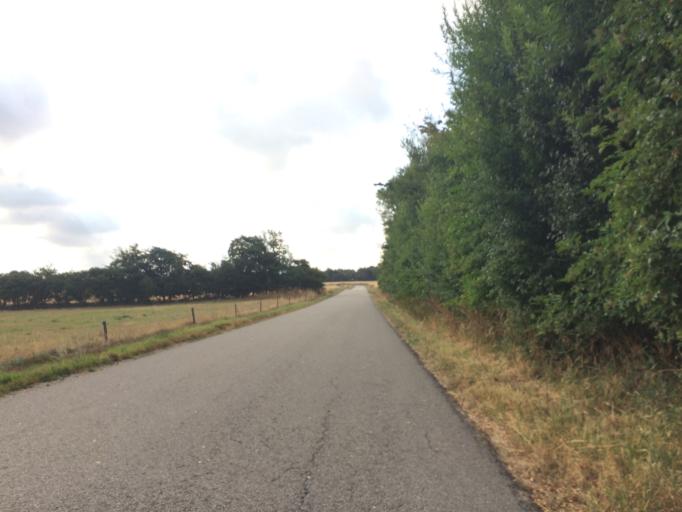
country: DK
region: Central Jutland
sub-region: Holstebro Kommune
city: Vinderup
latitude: 56.6083
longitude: 8.7857
